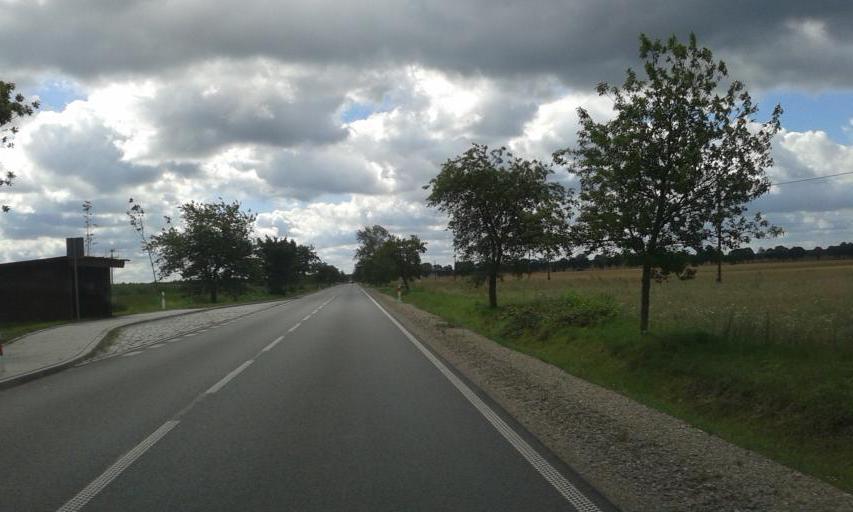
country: PL
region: West Pomeranian Voivodeship
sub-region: Powiat szczecinecki
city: Lubowo
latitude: 53.5018
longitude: 16.3289
